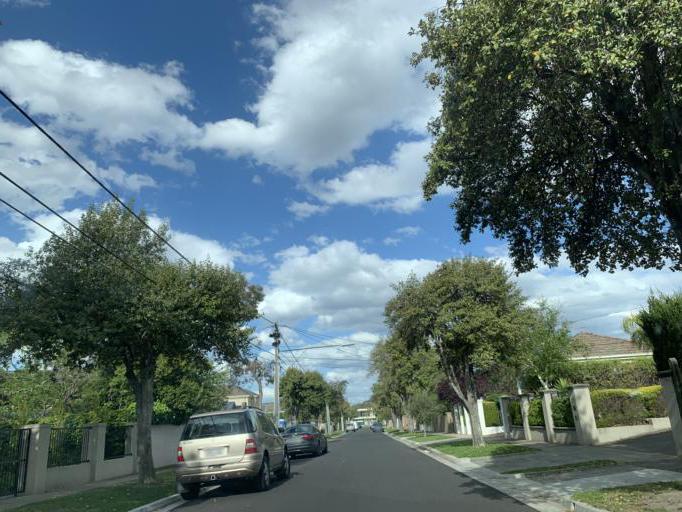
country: AU
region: Victoria
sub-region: Bayside
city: Hampton
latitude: -37.9255
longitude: 145.0082
